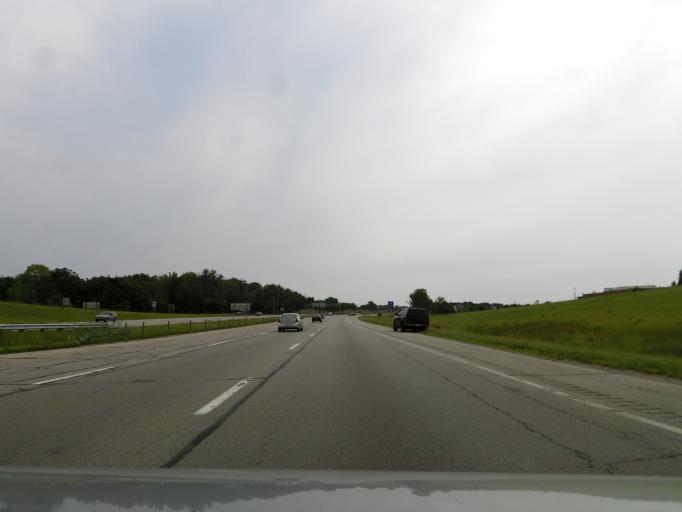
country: US
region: Ohio
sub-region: Montgomery County
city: Centerville
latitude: 39.6339
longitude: -84.1988
